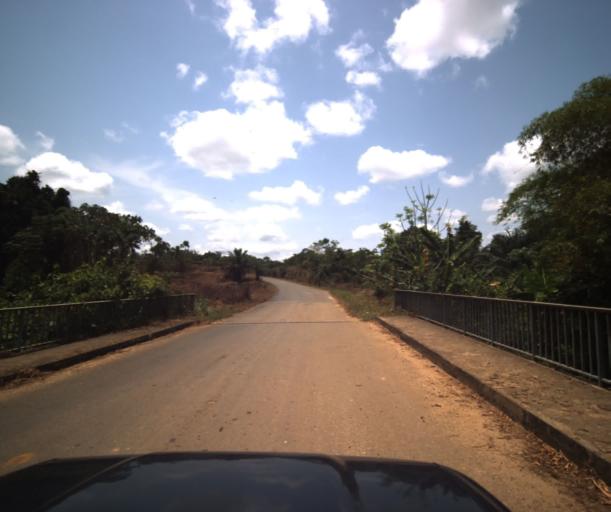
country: CM
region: Centre
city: Eseka
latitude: 3.7036
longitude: 10.7881
